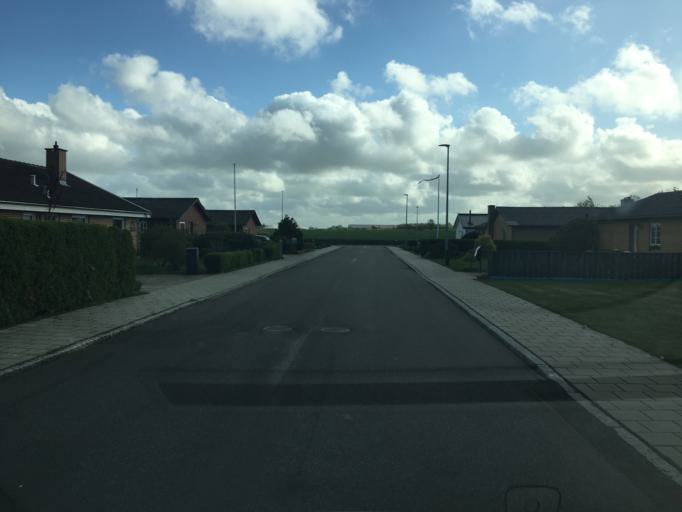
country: DK
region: South Denmark
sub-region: Tonder Kommune
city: Tonder
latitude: 55.0087
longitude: 8.7809
